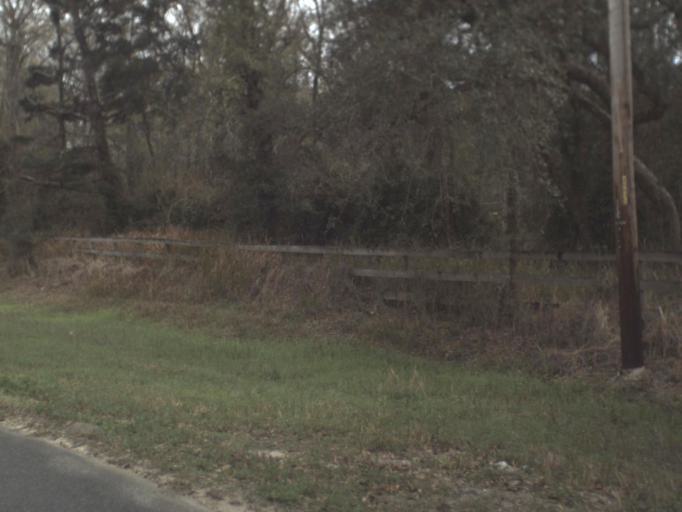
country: US
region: Florida
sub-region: Wakulla County
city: Crawfordville
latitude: 30.2518
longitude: -84.3214
